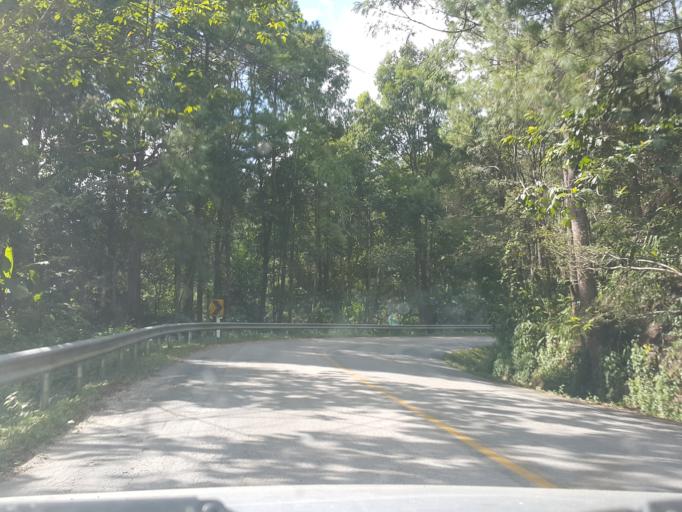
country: TH
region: Mae Hong Son
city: Mae Hi
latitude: 19.2619
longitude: 98.6377
